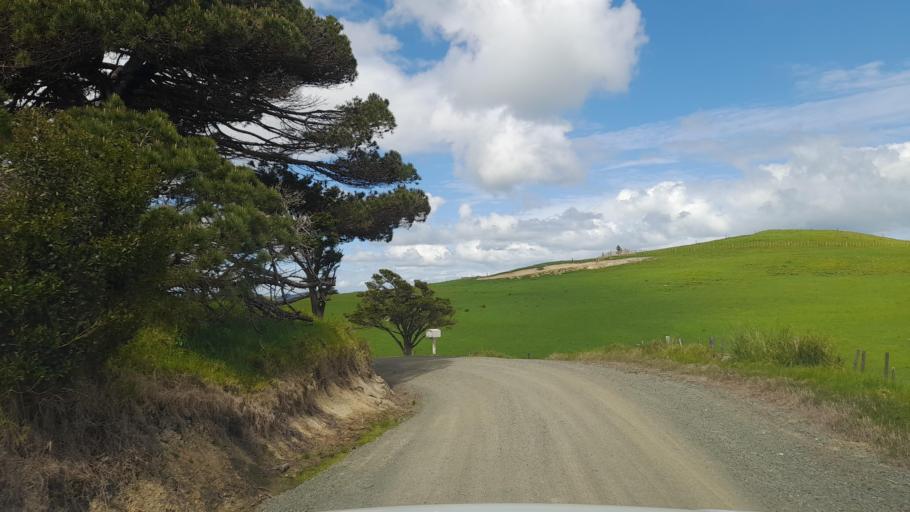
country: NZ
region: Auckland
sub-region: Auckland
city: Wellsford
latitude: -36.2163
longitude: 174.3201
